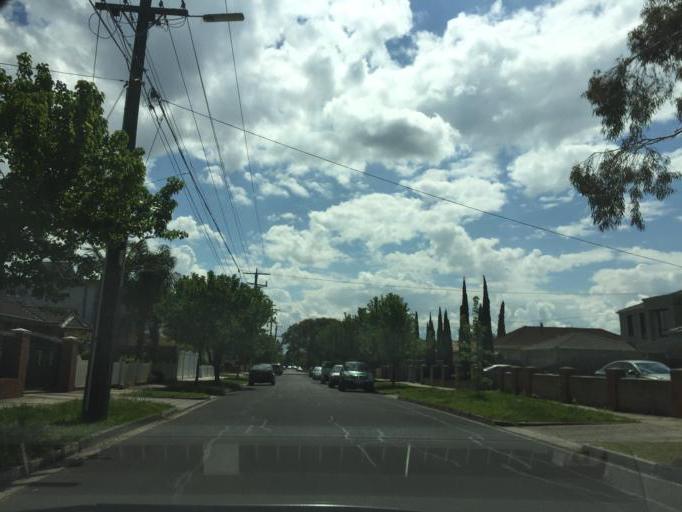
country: AU
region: Victoria
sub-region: Maribyrnong
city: Maidstone
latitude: -37.7889
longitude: 144.8713
